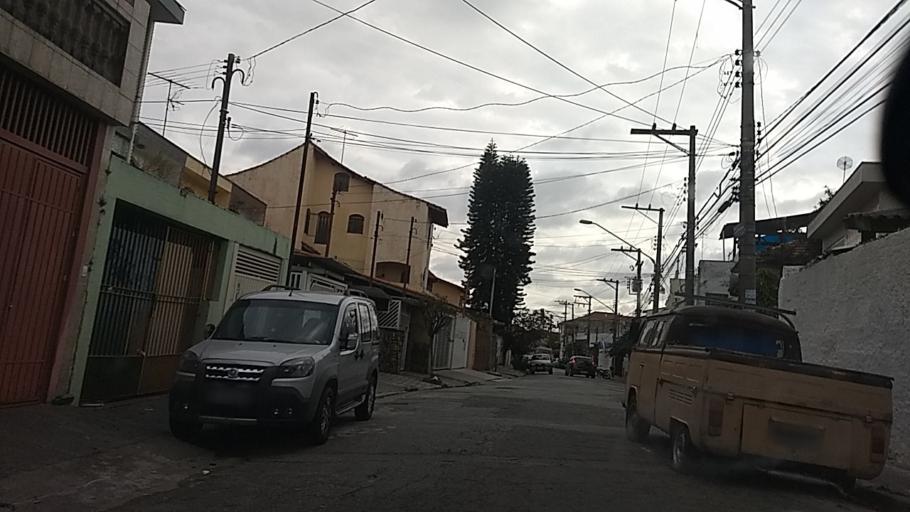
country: BR
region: Sao Paulo
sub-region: Sao Paulo
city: Sao Paulo
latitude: -23.5044
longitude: -46.5985
